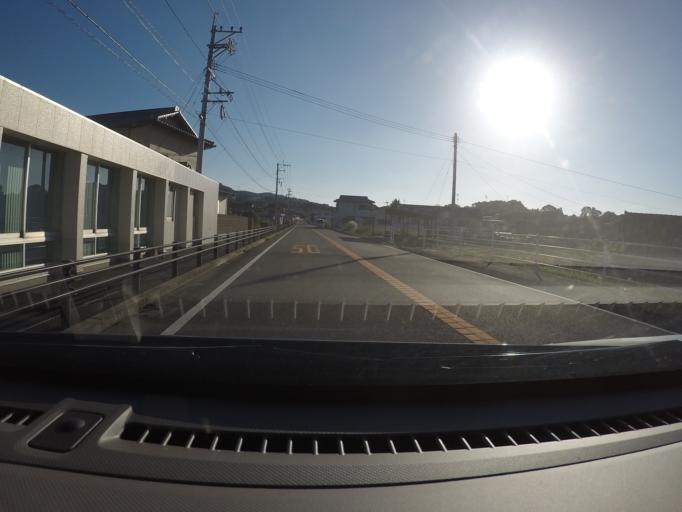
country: JP
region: Kumamoto
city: Minamata
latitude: 32.1761
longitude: 130.3836
